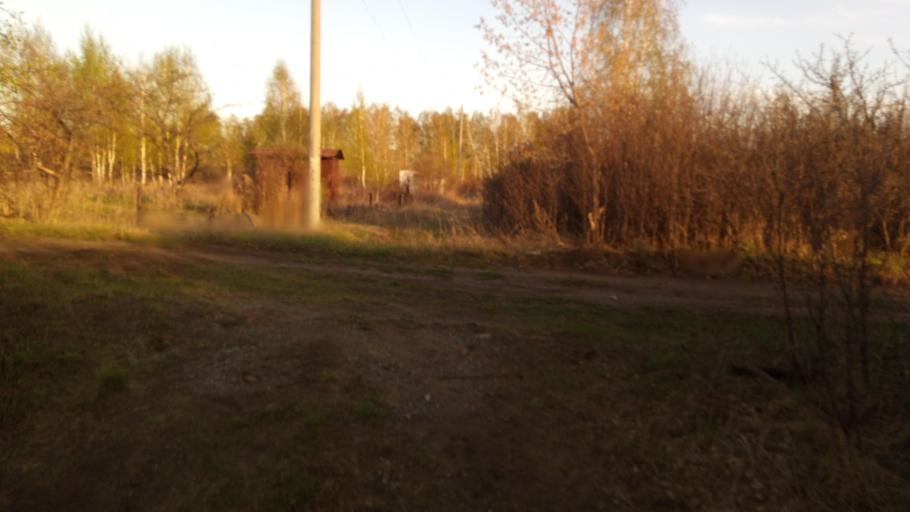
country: RU
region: Chelyabinsk
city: Timiryazevskiy
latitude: 54.9888
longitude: 60.8483
